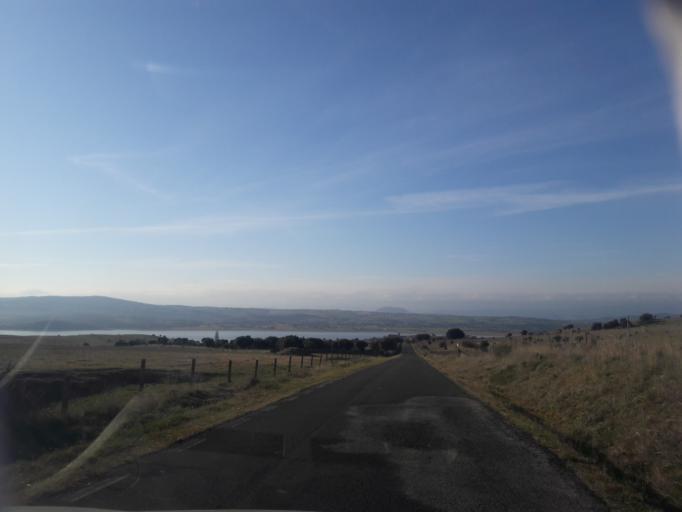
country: ES
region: Castille and Leon
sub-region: Provincia de Salamanca
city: Salvatierra de Tormes
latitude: 40.6034
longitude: -5.6004
